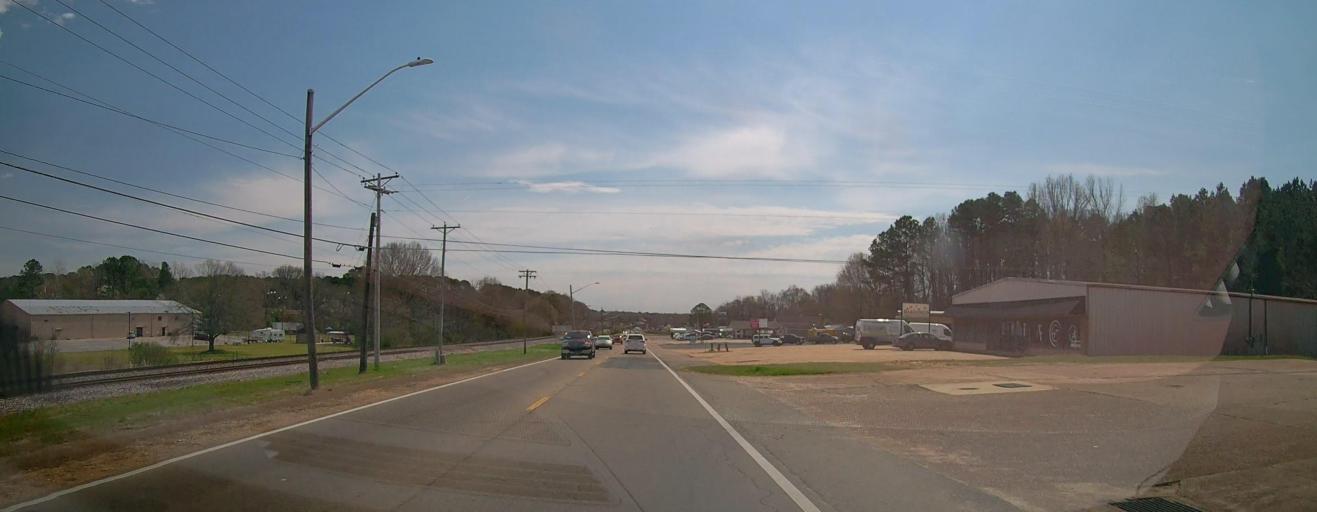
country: US
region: Mississippi
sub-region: Union County
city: New Albany
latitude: 34.5034
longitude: -89.0279
